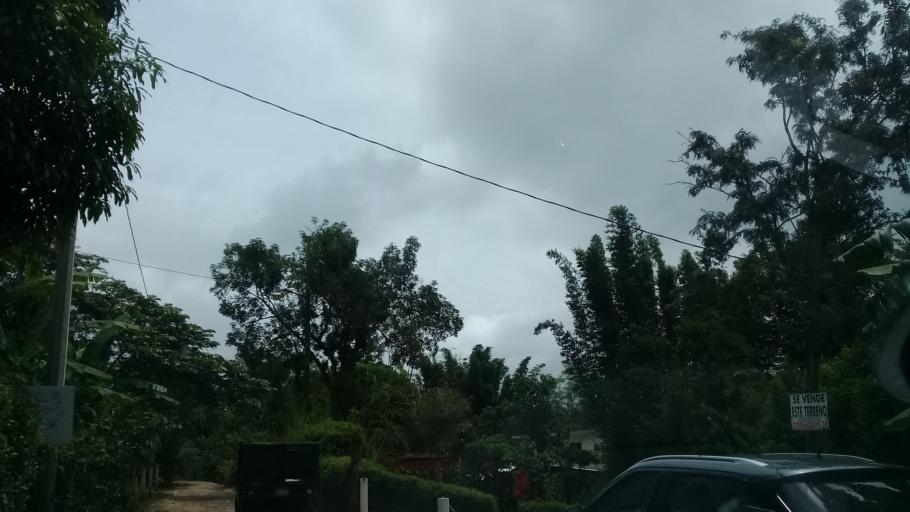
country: MX
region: Veracruz
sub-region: Xalapa
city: Colonia Santa Barbara
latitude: 19.4968
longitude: -96.8725
